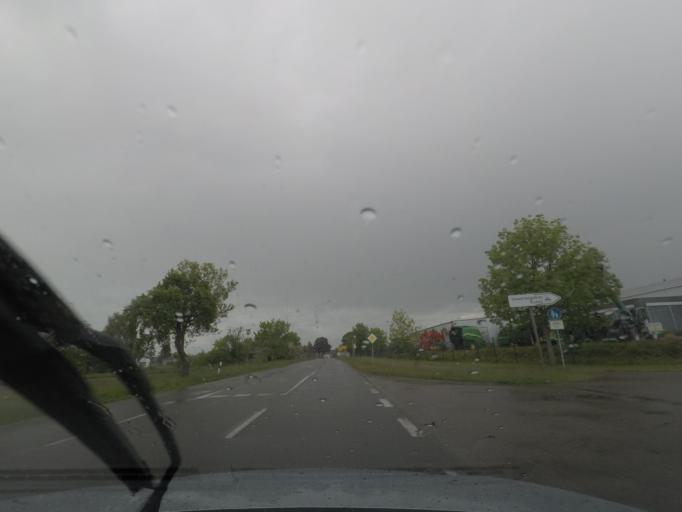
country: DE
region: Saxony-Anhalt
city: Kusey
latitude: 52.5759
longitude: 11.0889
